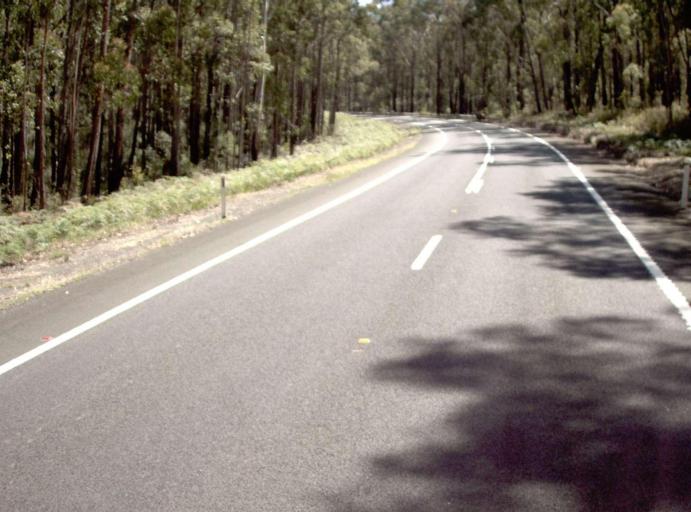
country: AU
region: New South Wales
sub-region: Bombala
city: Bombala
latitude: -37.5659
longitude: 149.0387
